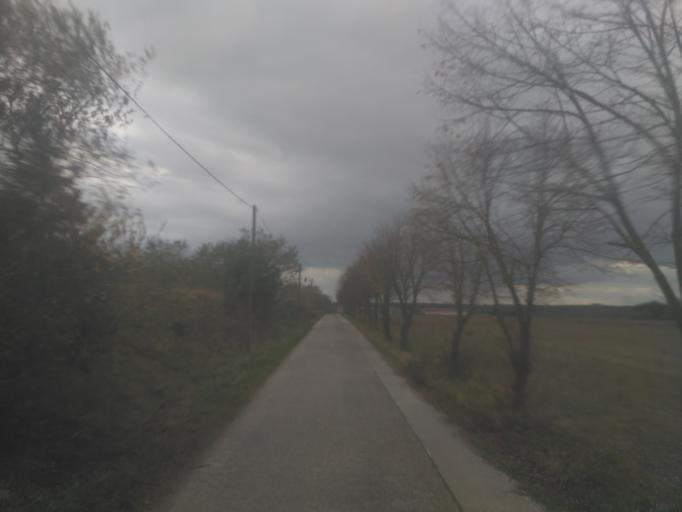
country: DE
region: Saxony
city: Zabeltitz
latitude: 51.3800
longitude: 13.5032
